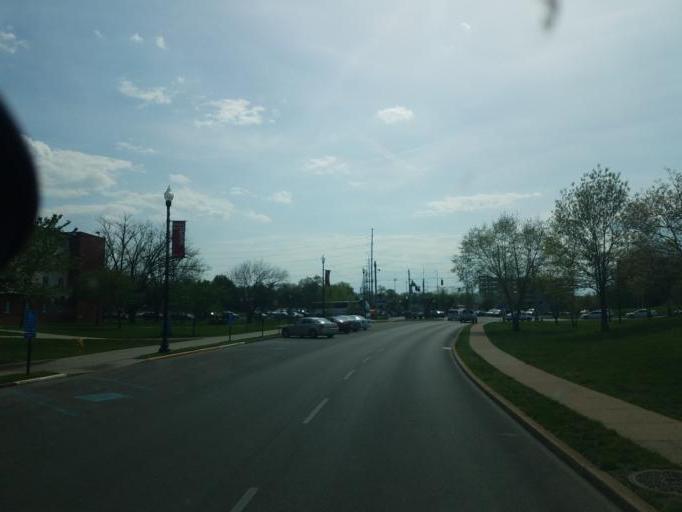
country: US
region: Kentucky
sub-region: Warren County
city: Bowling Green
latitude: 36.9824
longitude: -86.4608
